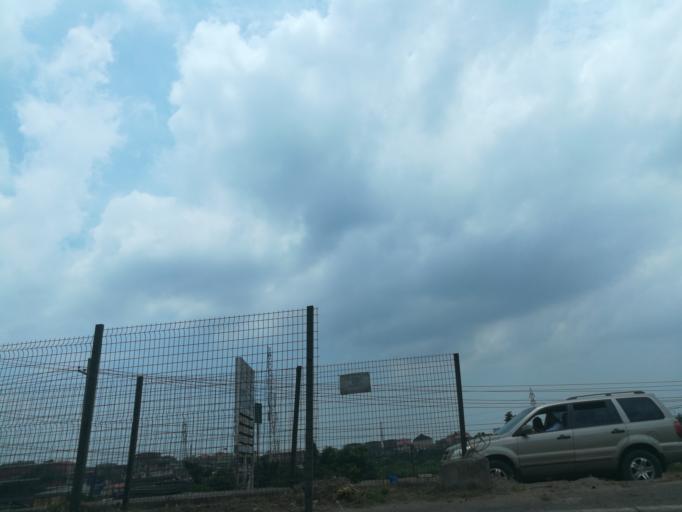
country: NG
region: Lagos
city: Ojota
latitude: 6.5823
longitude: 3.3748
